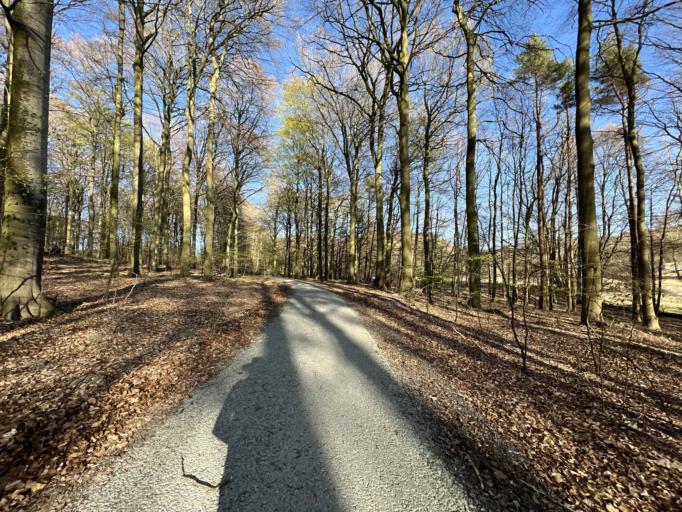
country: DE
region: Mecklenburg-Vorpommern
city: Sassnitz
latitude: 54.5299
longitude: 13.6398
